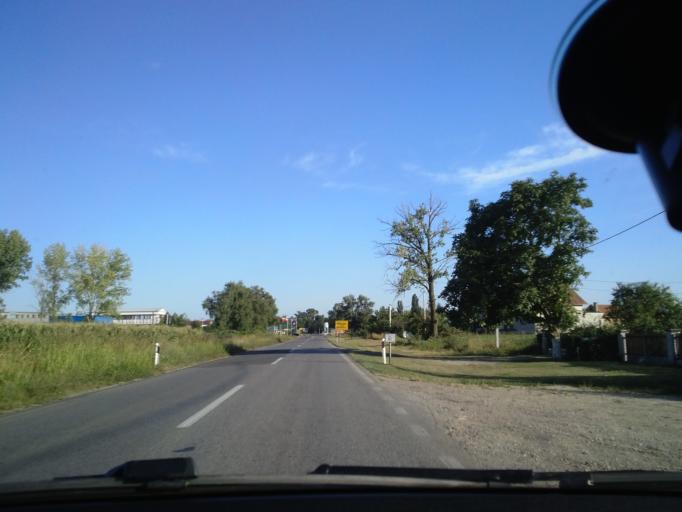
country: RS
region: Autonomna Pokrajina Vojvodina
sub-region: Zapadnobacki Okrug
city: Odzaci
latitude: 45.5183
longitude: 19.2465
